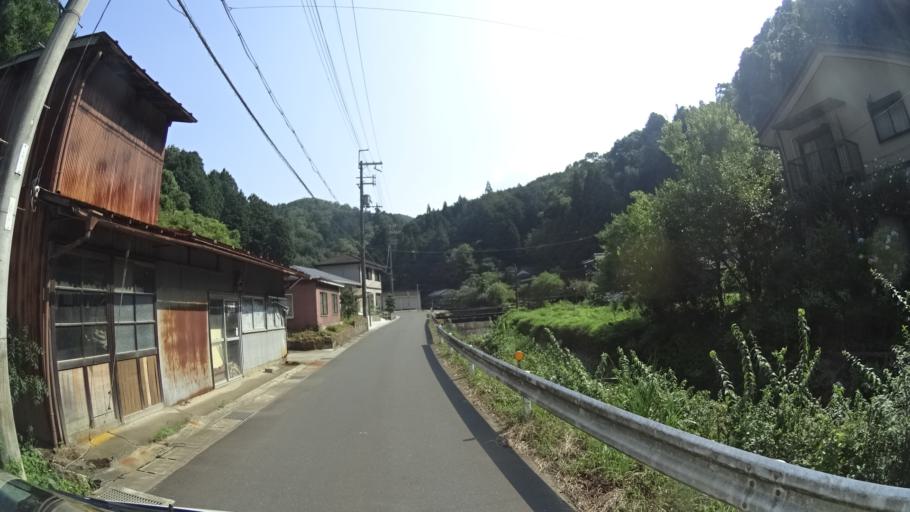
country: JP
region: Kyoto
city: Maizuru
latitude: 35.4222
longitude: 135.2223
